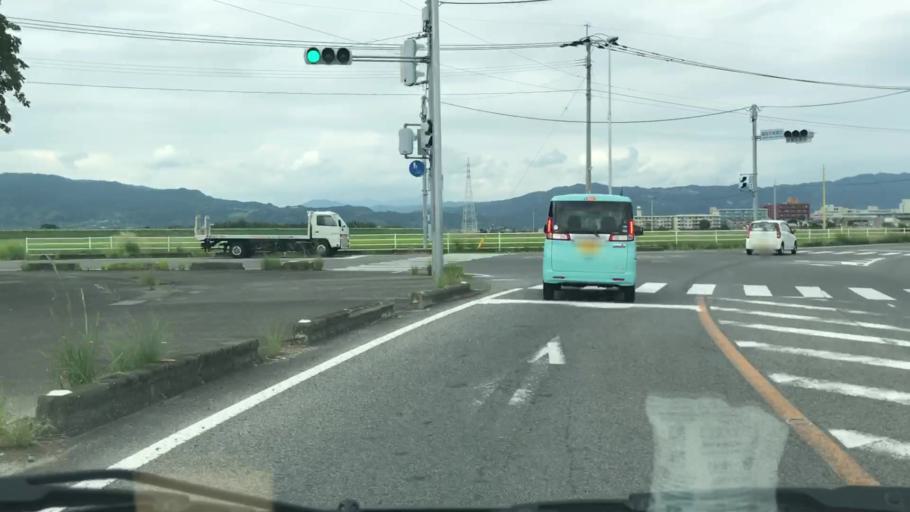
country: JP
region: Saga Prefecture
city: Saga-shi
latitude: 33.2757
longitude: 130.2606
